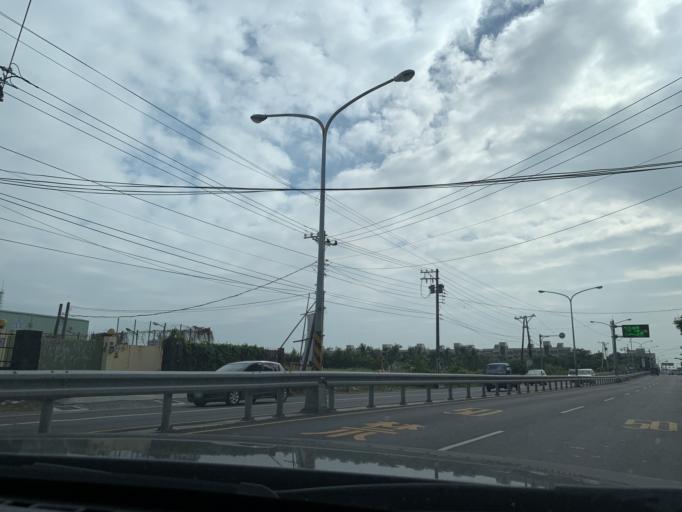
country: TW
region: Taiwan
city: Fengshan
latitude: 22.4660
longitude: 120.4631
